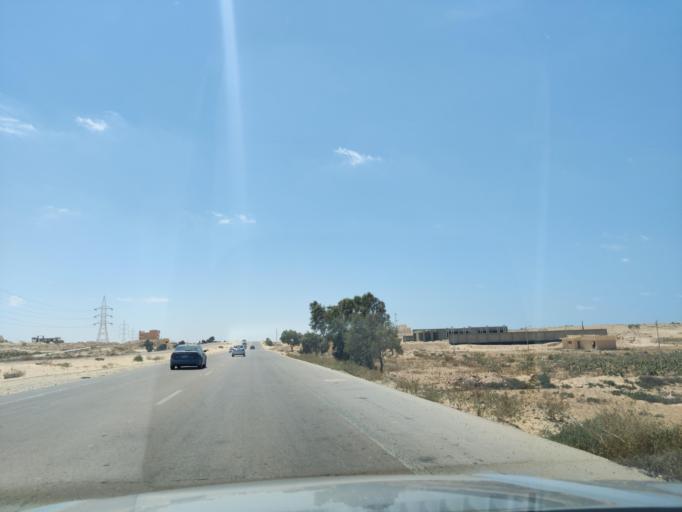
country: EG
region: Muhafazat Matruh
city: Al `Alamayn
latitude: 31.0702
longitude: 28.1537
